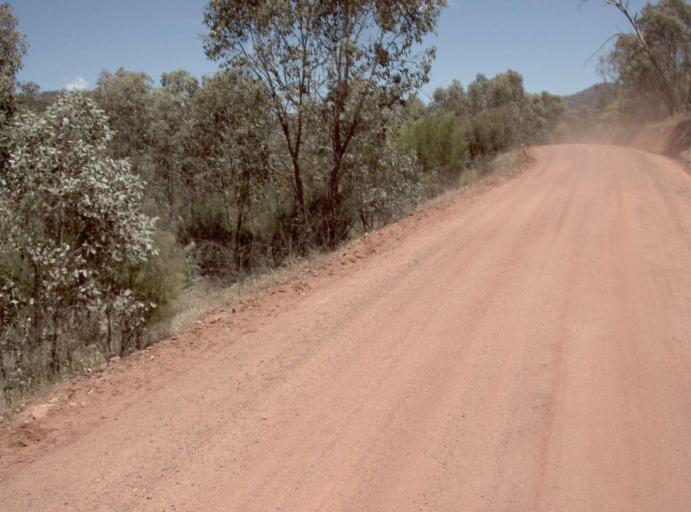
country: AU
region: New South Wales
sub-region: Snowy River
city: Jindabyne
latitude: -36.9179
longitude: 148.4205
